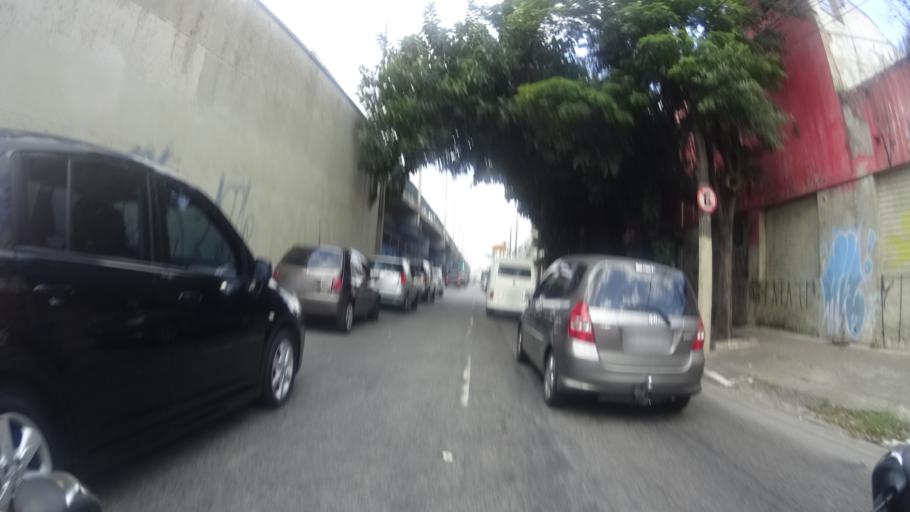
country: BR
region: Sao Paulo
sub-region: Sao Paulo
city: Sao Paulo
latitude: -23.5530
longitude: -46.6166
